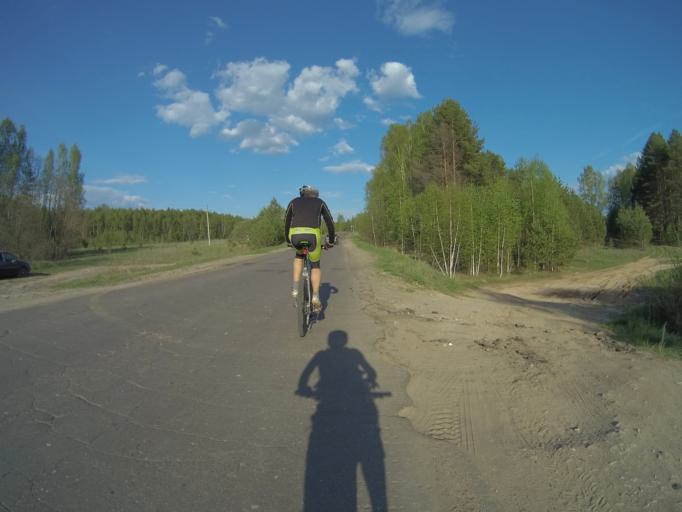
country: RU
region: Vladimir
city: Sudogda
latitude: 56.0742
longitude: 40.7810
